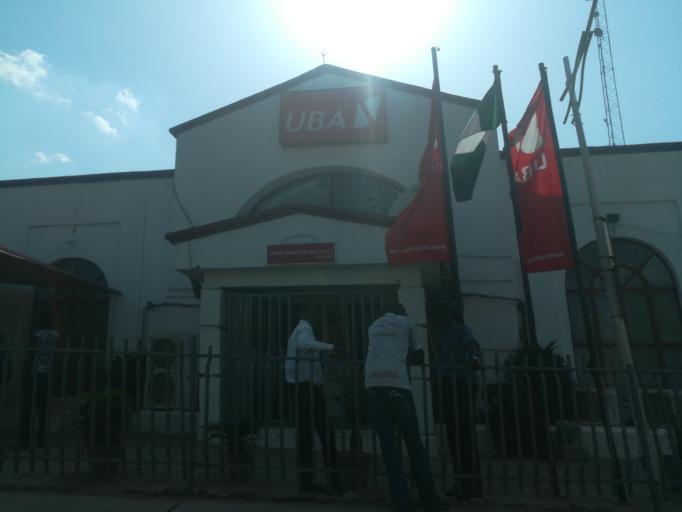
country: NG
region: Ogun
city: Abeokuta
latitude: 7.1379
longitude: 3.3322
